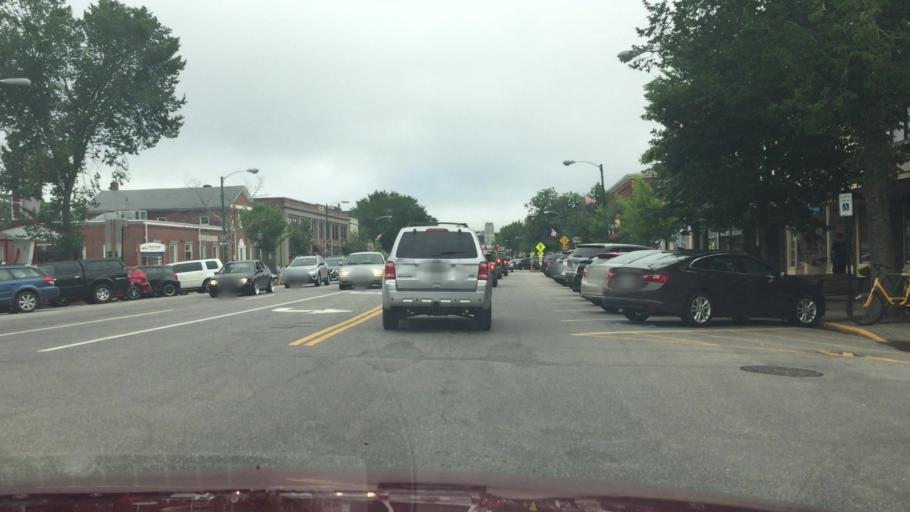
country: US
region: Maine
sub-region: Cumberland County
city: Brunswick
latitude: 43.9175
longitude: -69.9664
